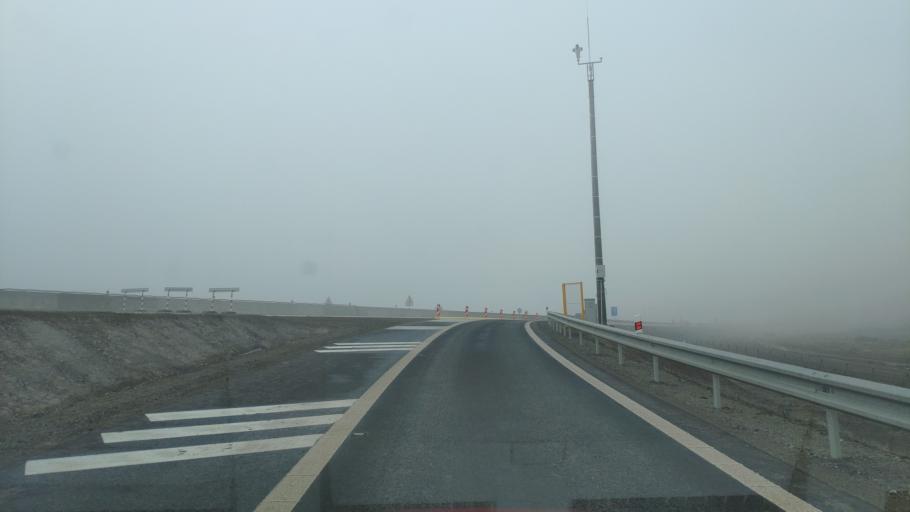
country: SK
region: Kosicky
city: Kosice
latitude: 48.7245
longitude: 21.4356
